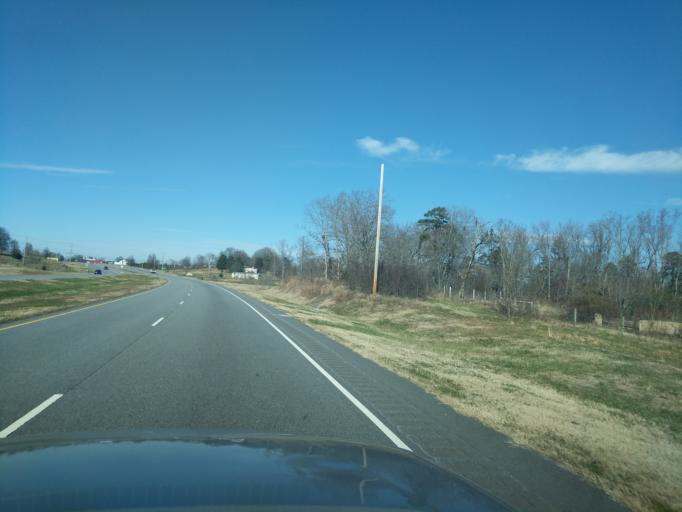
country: US
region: North Carolina
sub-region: Rutherford County
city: Forest City
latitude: 35.2317
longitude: -81.8446
